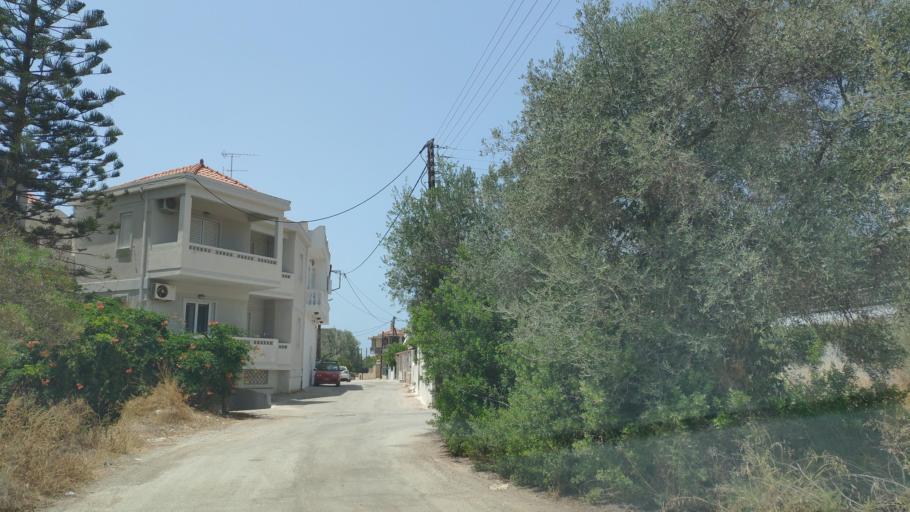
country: GR
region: Peloponnese
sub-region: Nomos Argolidos
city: Porto Cheli
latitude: 37.3294
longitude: 23.1484
